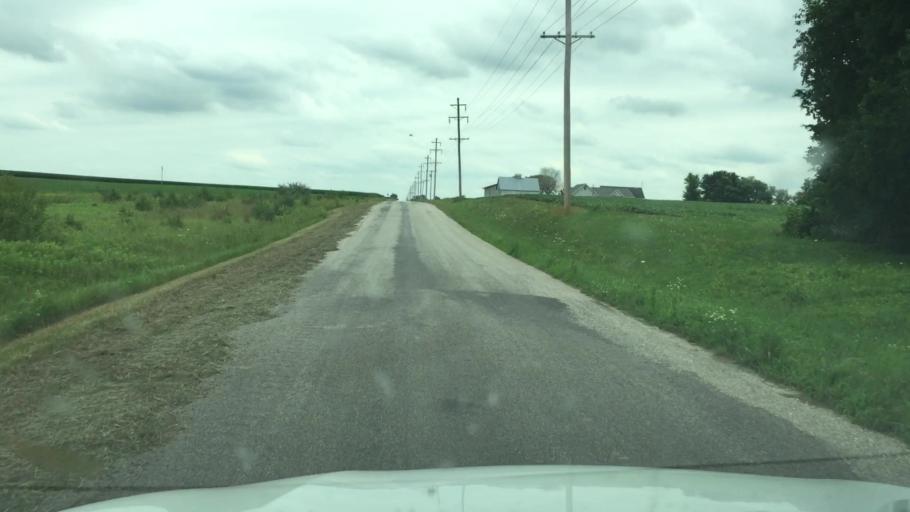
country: US
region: Illinois
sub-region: Hancock County
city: Carthage
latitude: 40.3452
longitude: -91.0822
